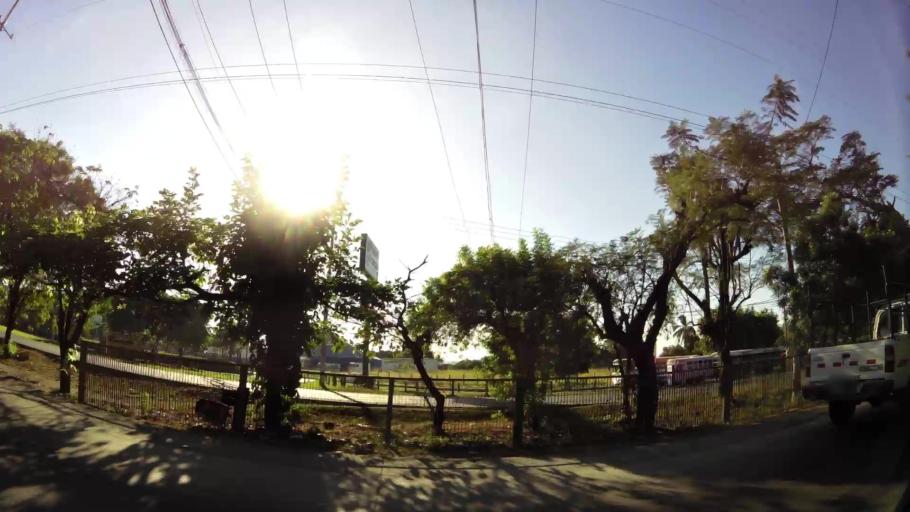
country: SV
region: La Libertad
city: Santa Tecla
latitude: 13.7307
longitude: -89.3591
